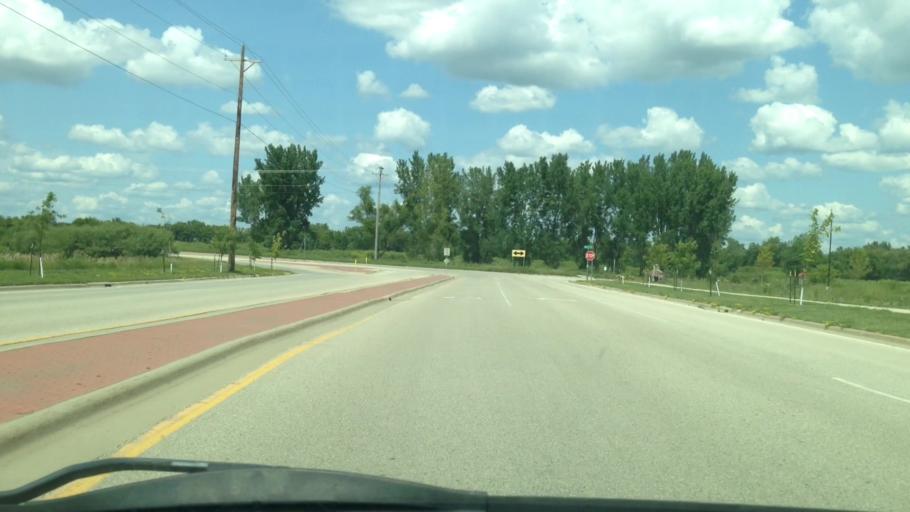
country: US
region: Minnesota
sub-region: Olmsted County
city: Rochester
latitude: 43.9627
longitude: -92.4584
